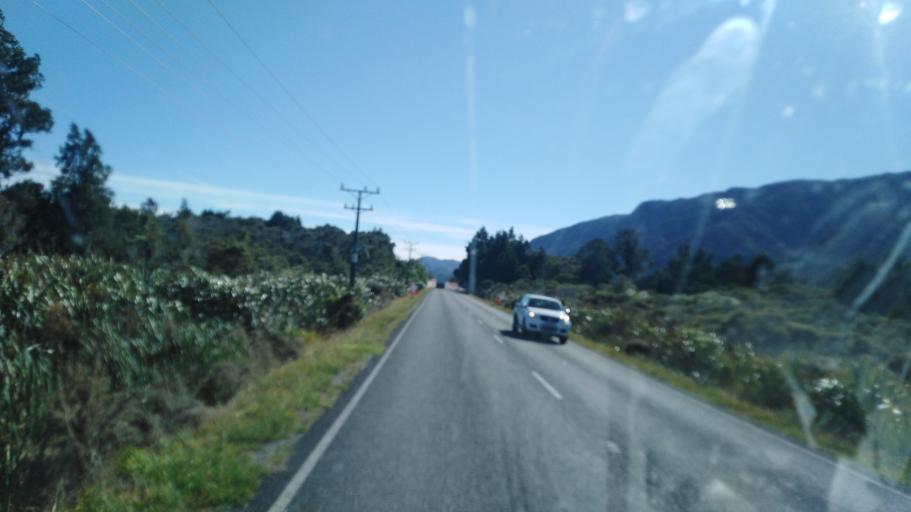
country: NZ
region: West Coast
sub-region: Buller District
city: Westport
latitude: -41.6696
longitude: 171.8064
